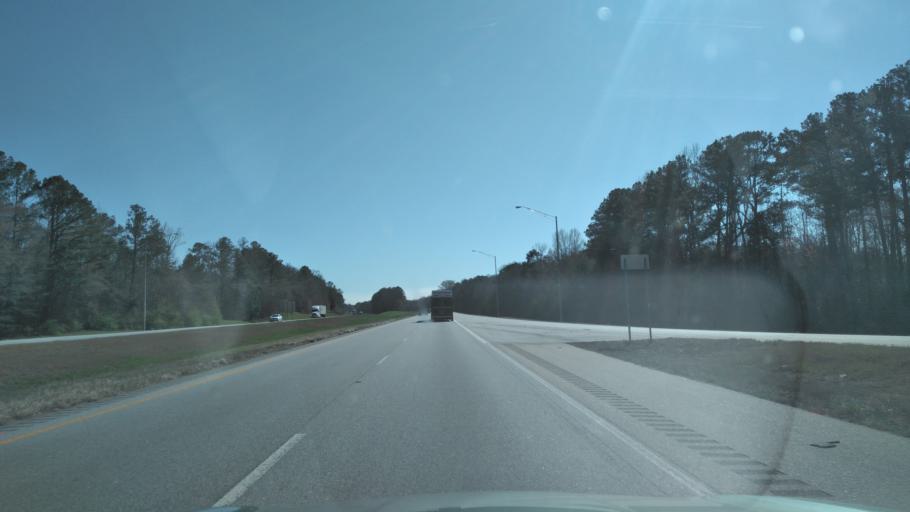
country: US
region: Alabama
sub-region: Lowndes County
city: Fort Deposit
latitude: 31.9830
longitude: -86.5309
